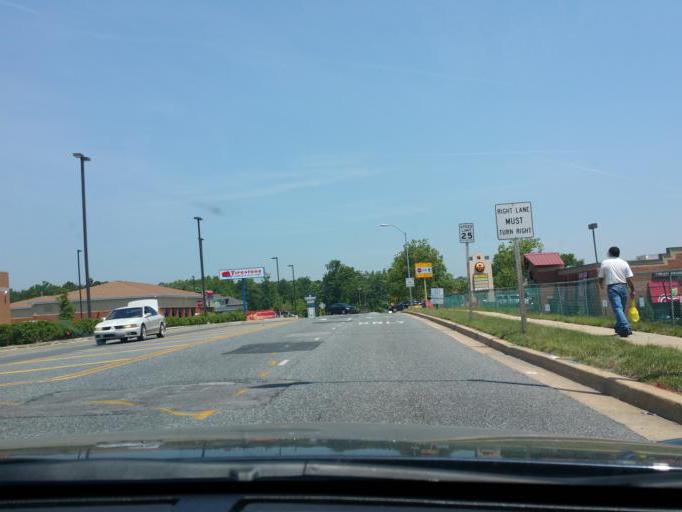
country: US
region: Maryland
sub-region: Harford County
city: Aberdeen
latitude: 39.5236
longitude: -76.1840
